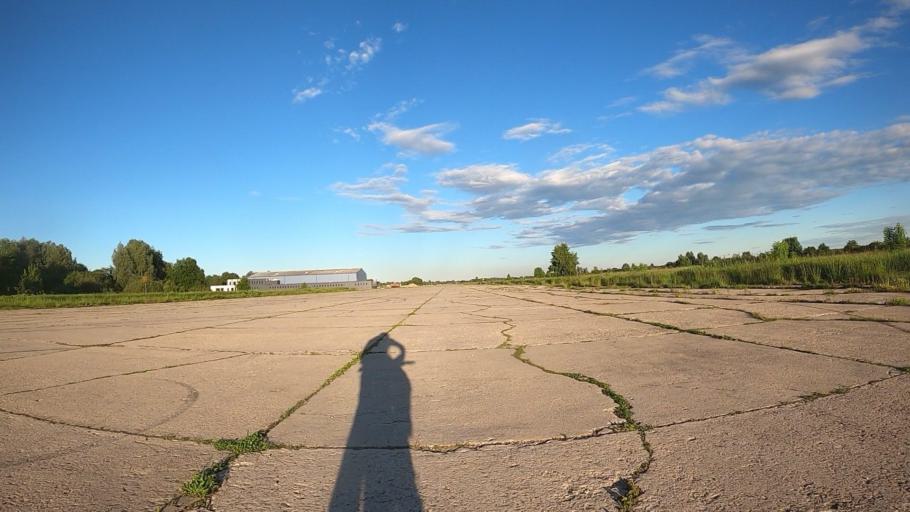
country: LV
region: Kekava
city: Kekava
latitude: 56.8868
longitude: 24.2167
